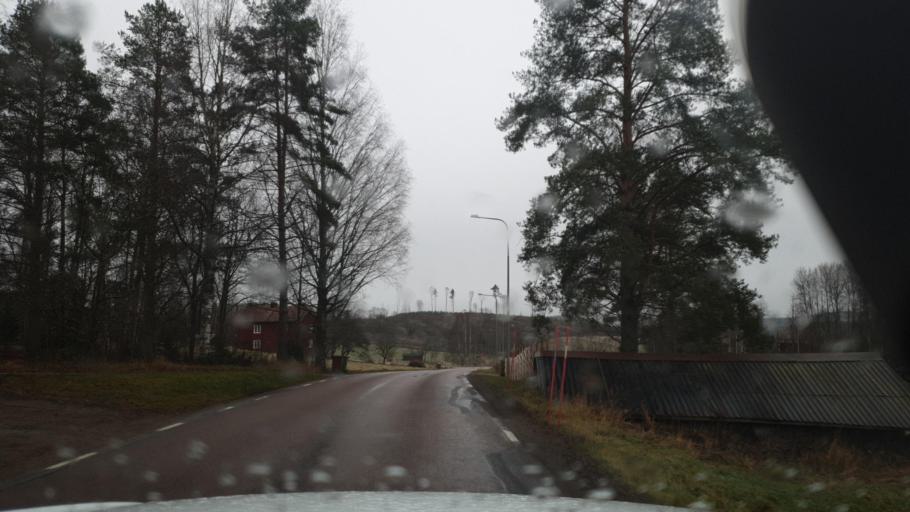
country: SE
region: Vaermland
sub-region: Arvika Kommun
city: Arvika
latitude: 59.6863
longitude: 12.7875
